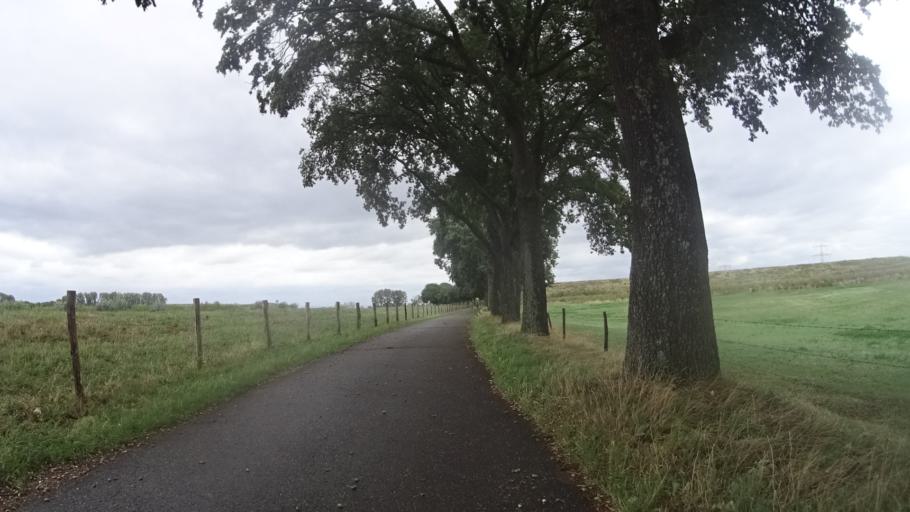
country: NL
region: Limburg
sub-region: Gemeente Sittard-Geleen
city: Born
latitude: 51.0475
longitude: 5.7879
